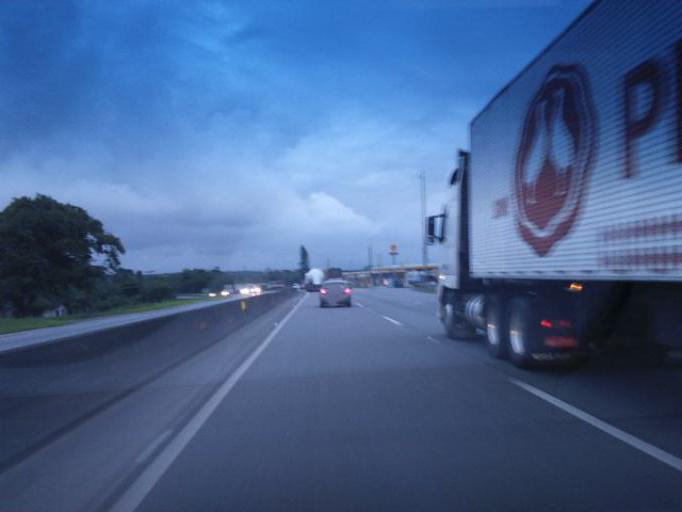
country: BR
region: Santa Catarina
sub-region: Barra Velha
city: Barra Velha
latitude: -26.5533
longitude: -48.7184
